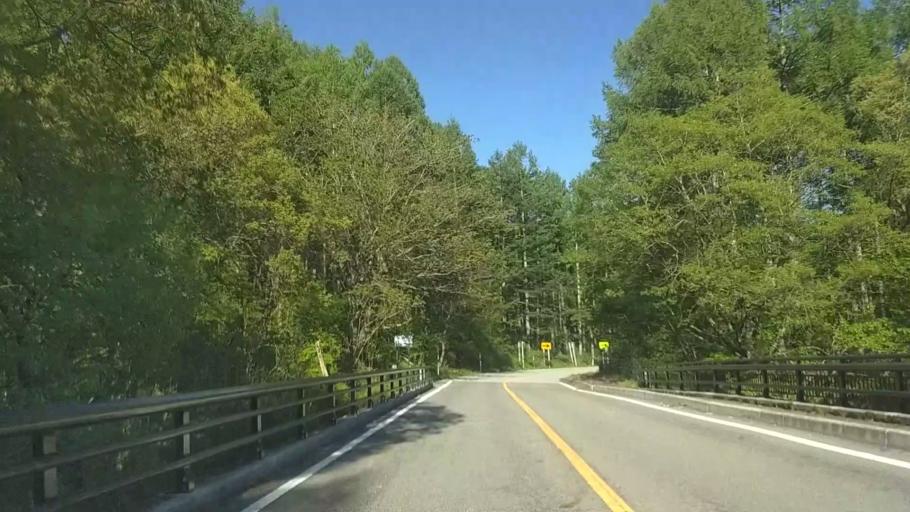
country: JP
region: Nagano
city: Chino
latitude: 35.9002
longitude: 138.3540
